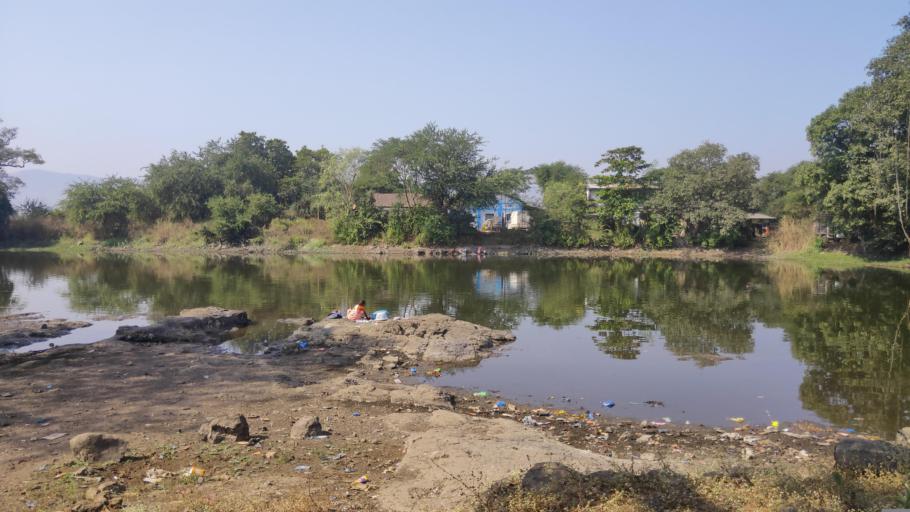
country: IN
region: Maharashtra
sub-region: Thane
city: Bhiwandi
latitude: 19.3337
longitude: 73.0210
